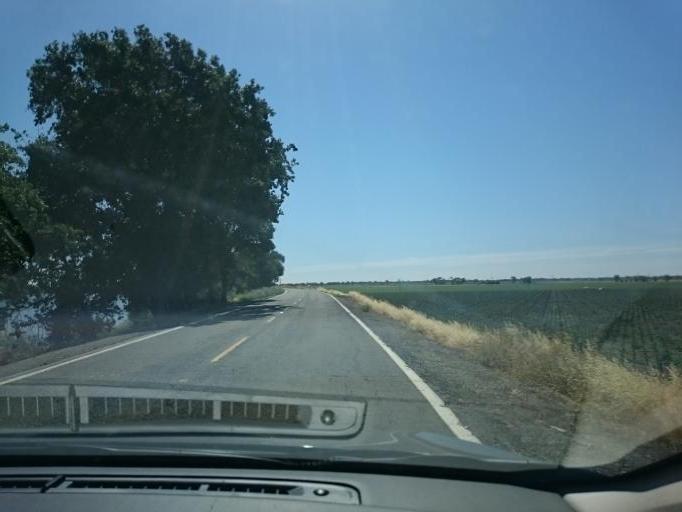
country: US
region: California
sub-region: Sacramento County
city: Parkway
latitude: 38.4736
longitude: -121.5389
